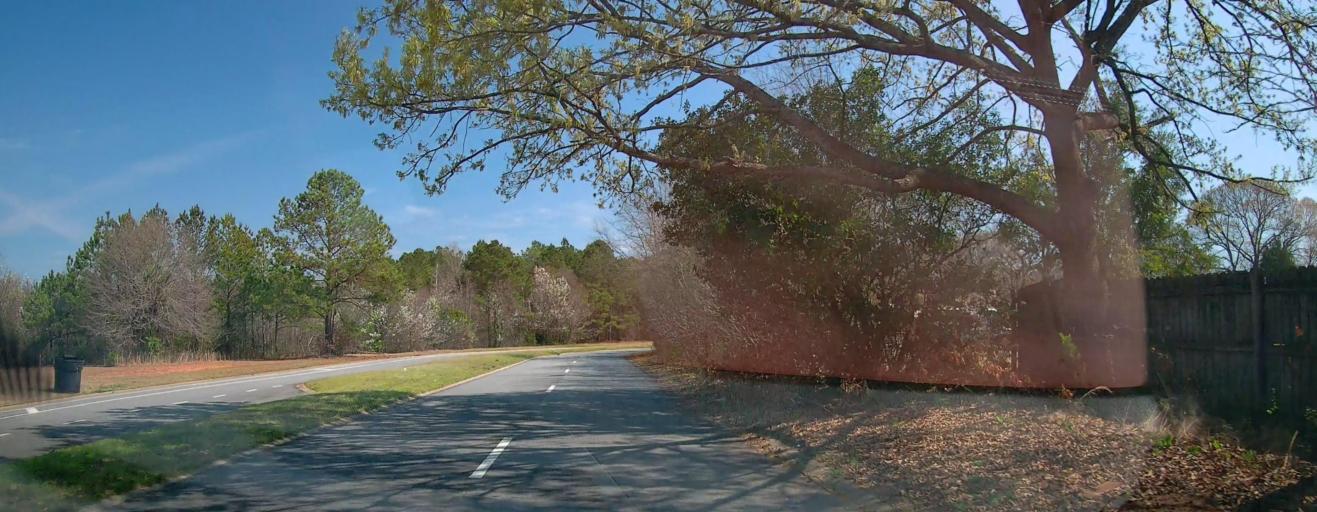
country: US
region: Georgia
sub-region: Houston County
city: Centerville
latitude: 32.6143
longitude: -83.6776
